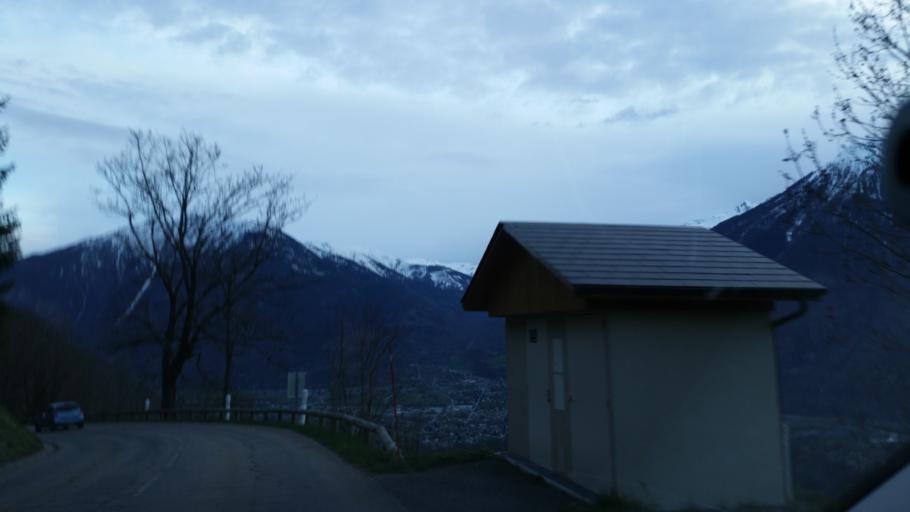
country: FR
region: Rhone-Alpes
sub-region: Departement de la Savoie
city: La Chambre
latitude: 45.3751
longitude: 6.3233
